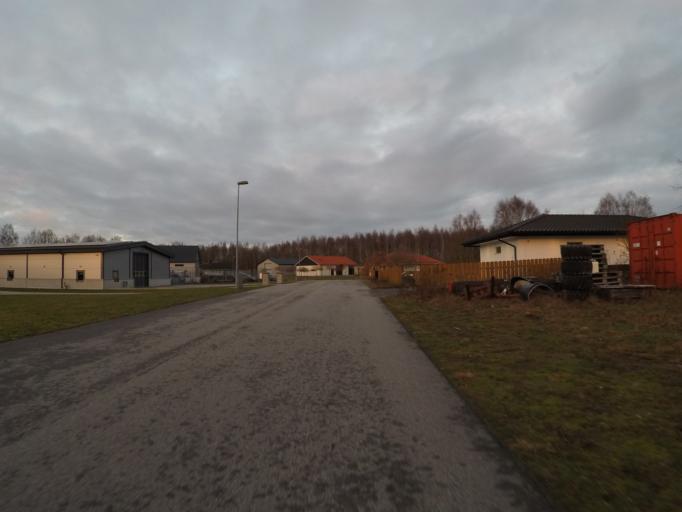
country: SE
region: Skane
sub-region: Sjobo Kommun
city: Sjoebo
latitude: 55.6443
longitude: 13.6952
